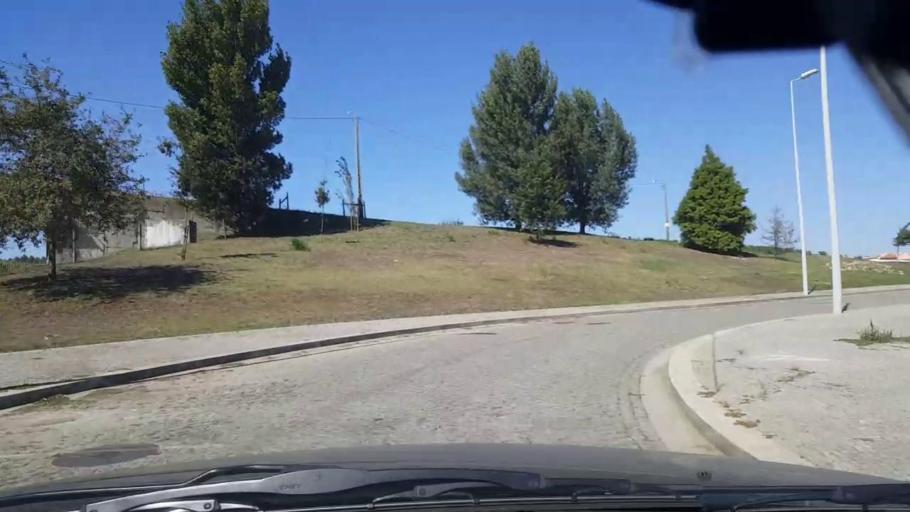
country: PT
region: Porto
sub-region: Matosinhos
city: Lavra
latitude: 41.2857
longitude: -8.6937
